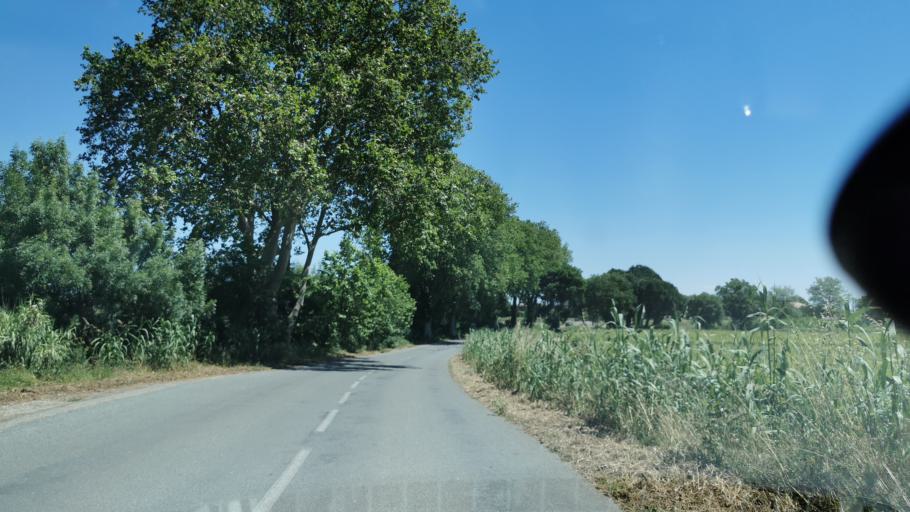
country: FR
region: Languedoc-Roussillon
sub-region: Departement de l'Aude
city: Saint-Marcel-sur-Aude
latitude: 43.2565
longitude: 2.9382
